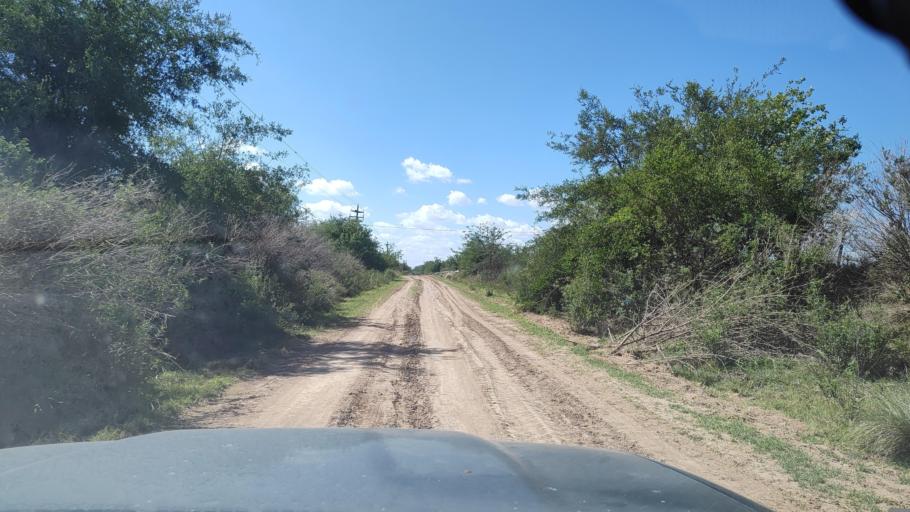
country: AR
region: Buenos Aires
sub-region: Partido de Lujan
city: Lujan
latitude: -34.5237
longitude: -59.1565
